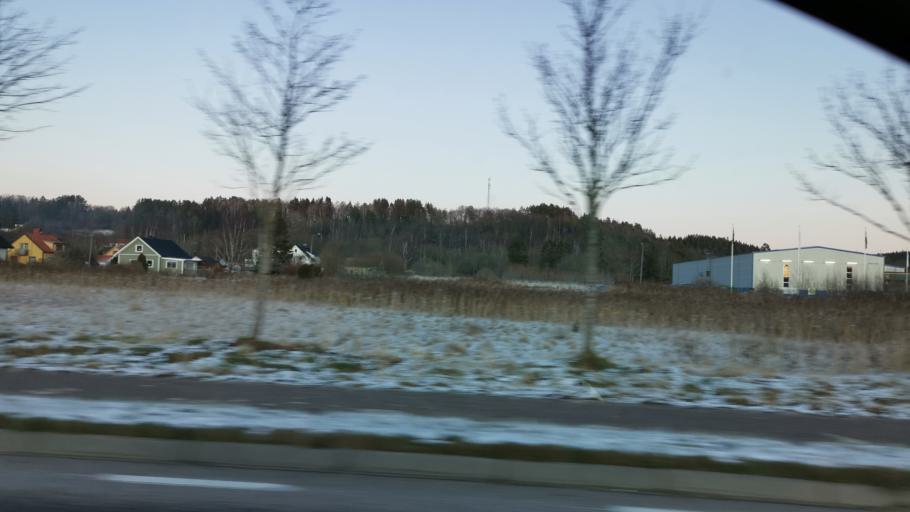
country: SE
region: Vaestra Goetaland
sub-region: Munkedals Kommun
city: Munkedal
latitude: 58.3958
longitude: 11.7549
